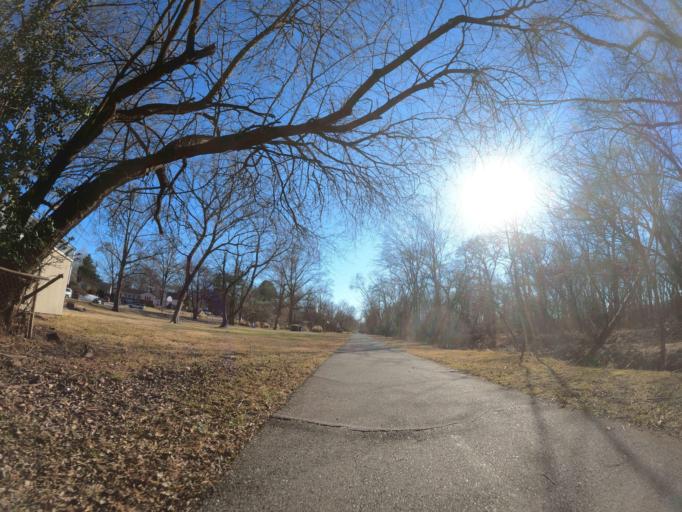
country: US
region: Maryland
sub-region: Prince George's County
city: Berwyn Heights
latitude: 38.9960
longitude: -76.9180
